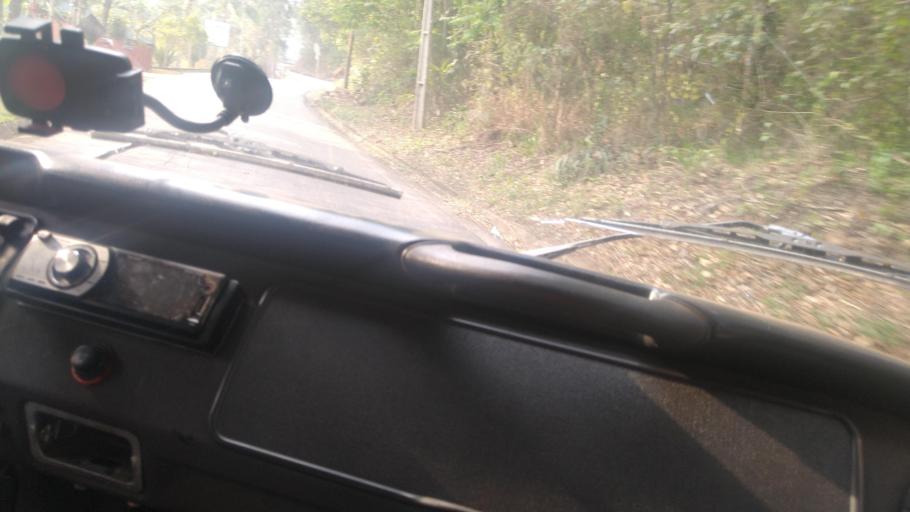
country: BR
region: Minas Gerais
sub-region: Extrema
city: Extrema
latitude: -22.7717
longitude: -46.4374
